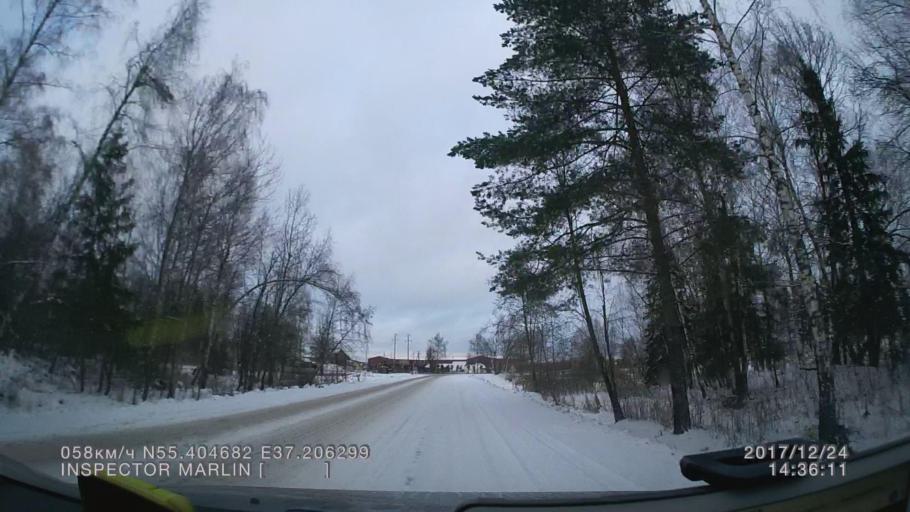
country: RU
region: Moskovskaya
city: Troitsk
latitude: 55.4046
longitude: 37.2062
